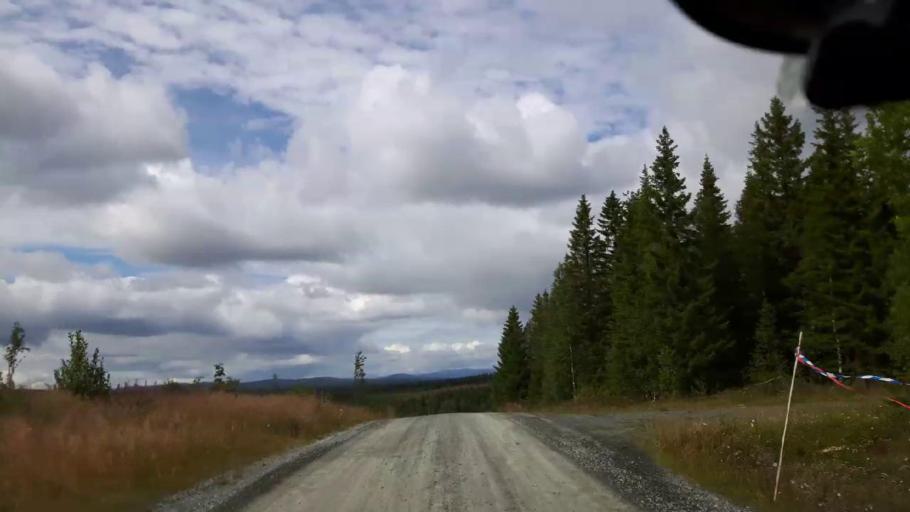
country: SE
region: Jaemtland
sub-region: Krokoms Kommun
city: Valla
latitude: 63.5722
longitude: 13.9131
